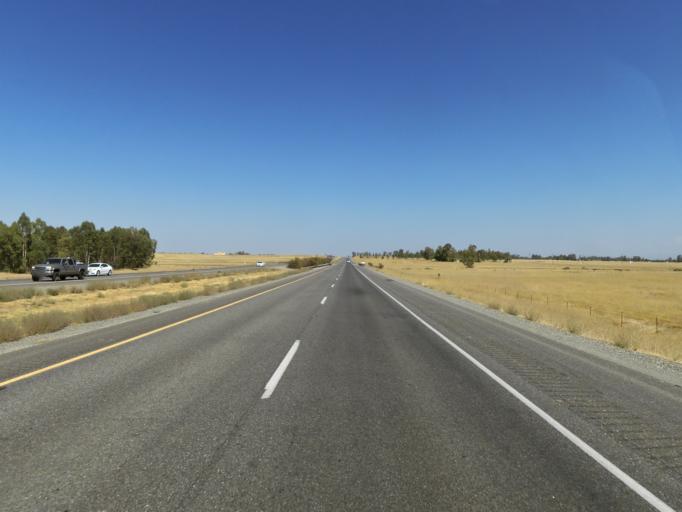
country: US
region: California
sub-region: Tehama County
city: Corning
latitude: 39.8544
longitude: -122.1999
